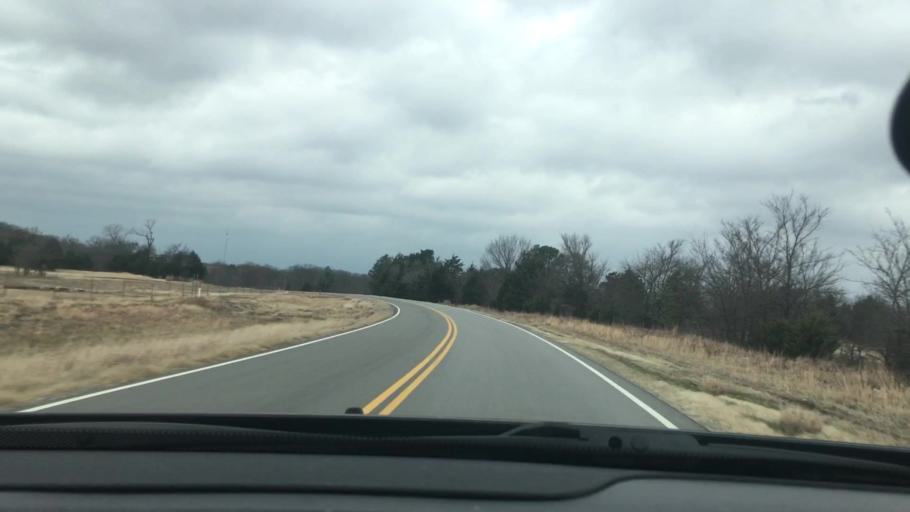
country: US
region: Oklahoma
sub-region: Atoka County
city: Atoka
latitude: 34.3782
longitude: -96.2642
